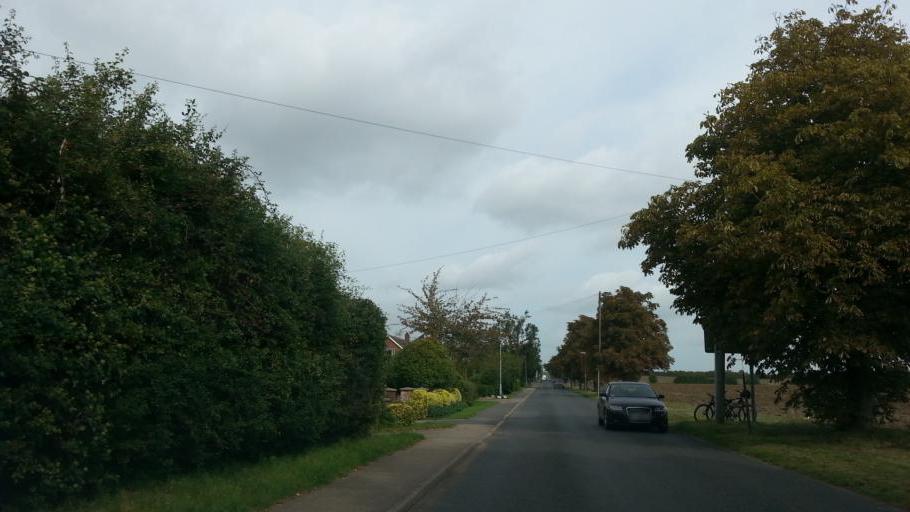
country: GB
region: England
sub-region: Cambridgeshire
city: Comberton
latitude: 52.1885
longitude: 0.0297
